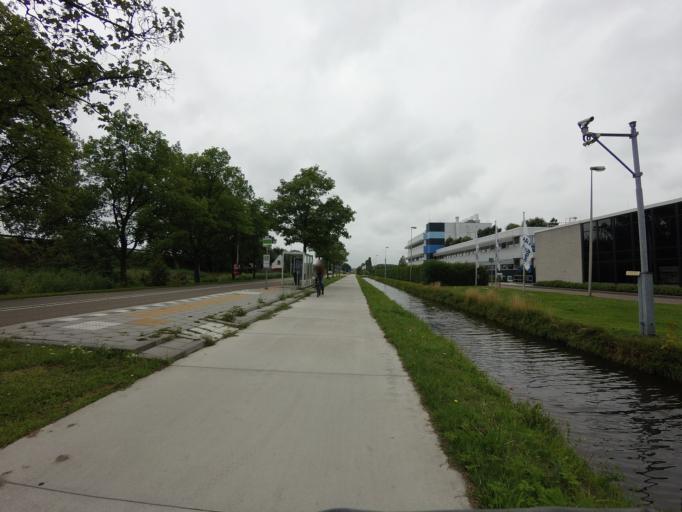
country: NL
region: South Holland
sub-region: Gemeente Teylingen
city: Voorhout
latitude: 52.2060
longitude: 4.4883
